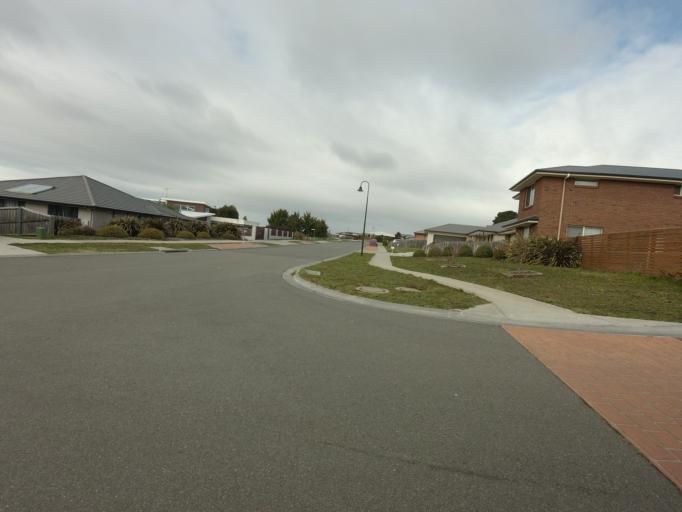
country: AU
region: Tasmania
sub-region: Clarence
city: Howrah
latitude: -42.8847
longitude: 147.4243
